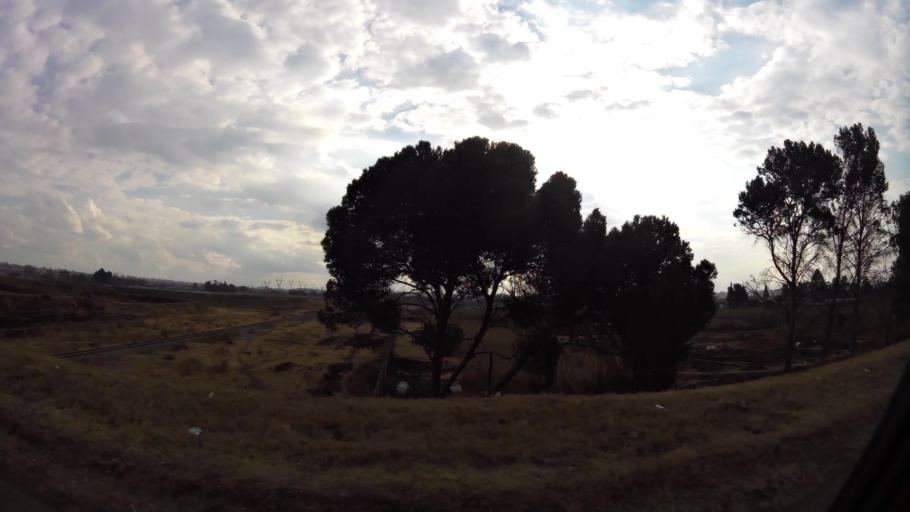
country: ZA
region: Gauteng
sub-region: Sedibeng District Municipality
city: Vereeniging
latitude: -26.6750
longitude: 27.8978
